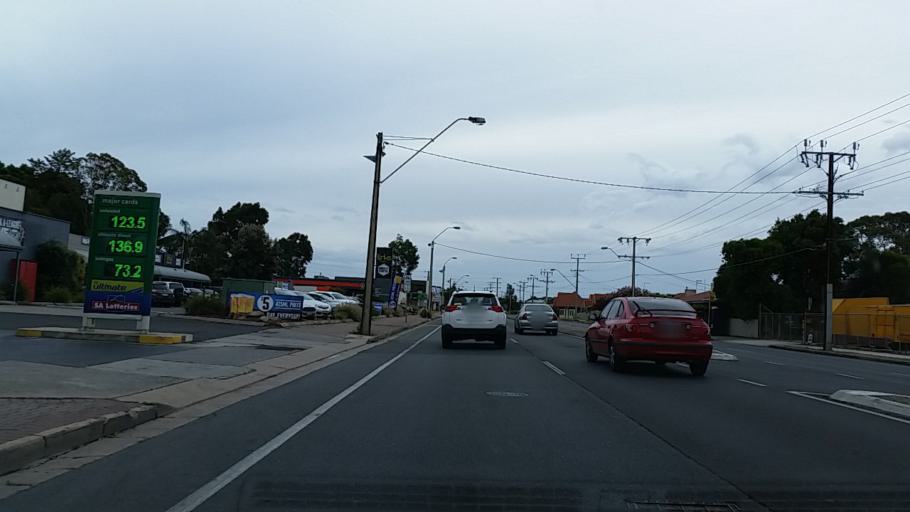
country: AU
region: South Australia
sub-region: Charles Sturt
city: Seaton
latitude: -34.9020
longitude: 138.5144
